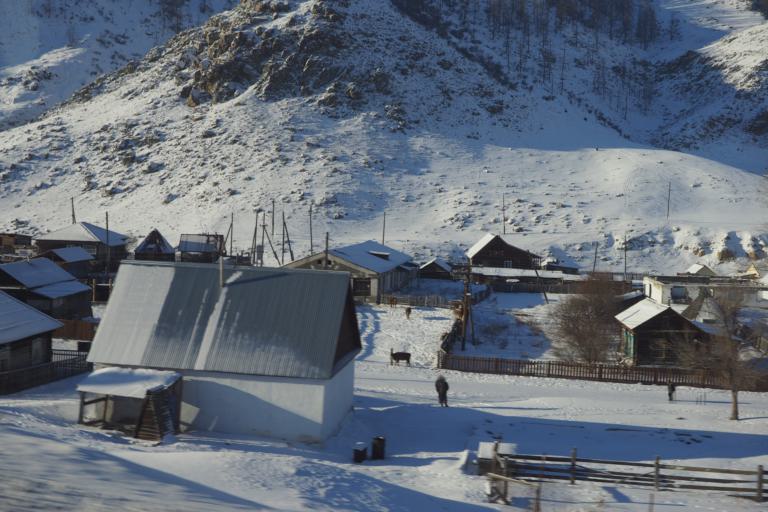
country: RU
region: Altay
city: Onguday
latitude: 50.6836
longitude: 86.2879
